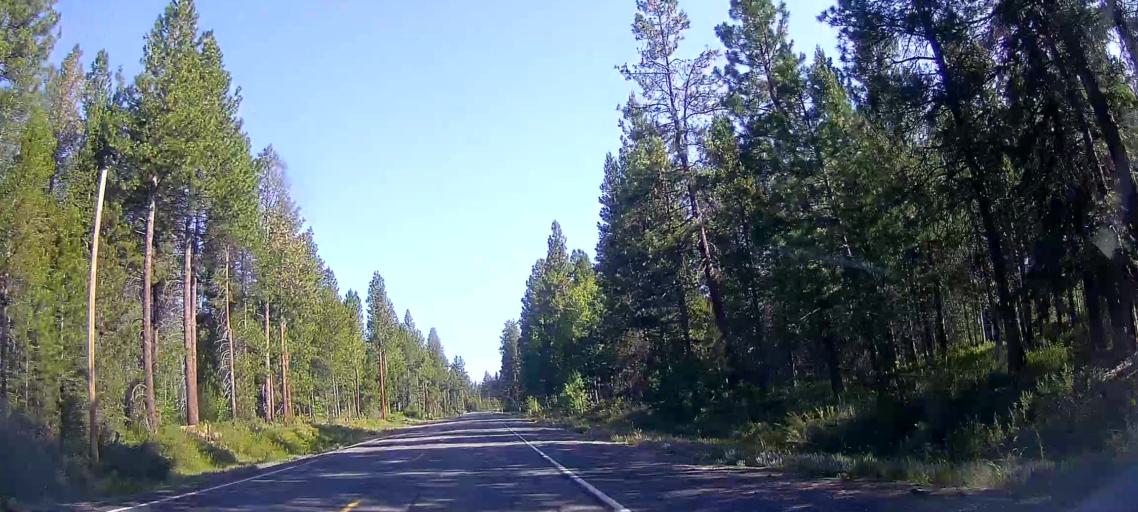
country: US
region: Oregon
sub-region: Klamath County
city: Klamath Falls
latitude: 42.6792
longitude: -121.9719
